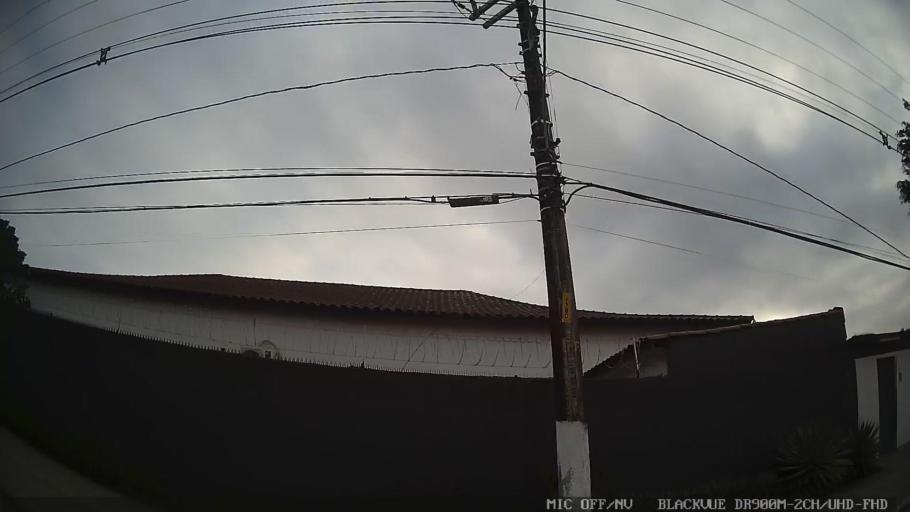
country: BR
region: Sao Paulo
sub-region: Guaruja
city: Guaruja
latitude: -23.9780
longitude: -46.2096
